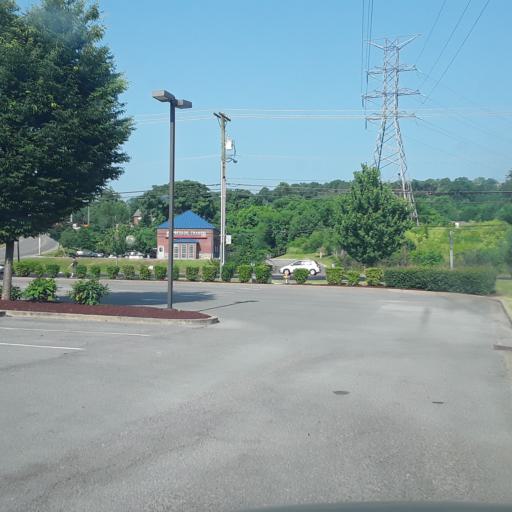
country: US
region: Tennessee
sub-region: Williamson County
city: Brentwood Estates
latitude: 36.0433
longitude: -86.7122
